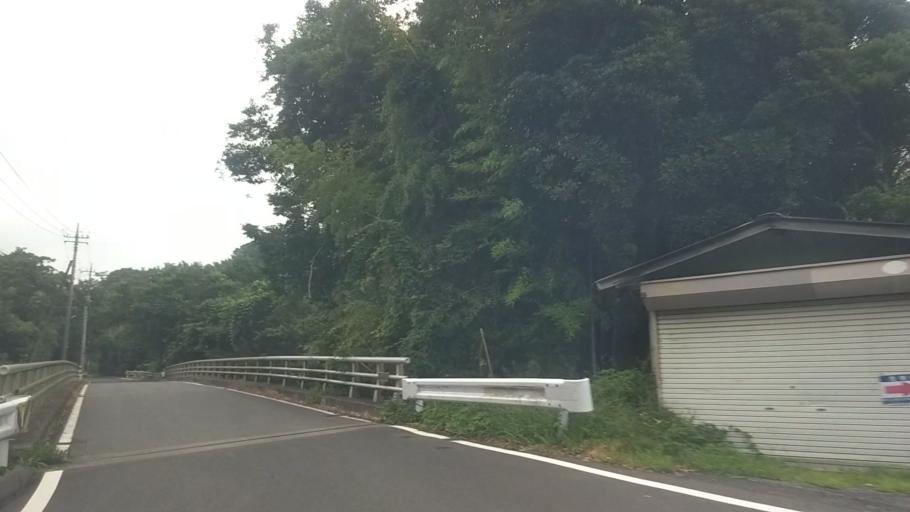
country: JP
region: Chiba
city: Kawaguchi
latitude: 35.2574
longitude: 140.0492
